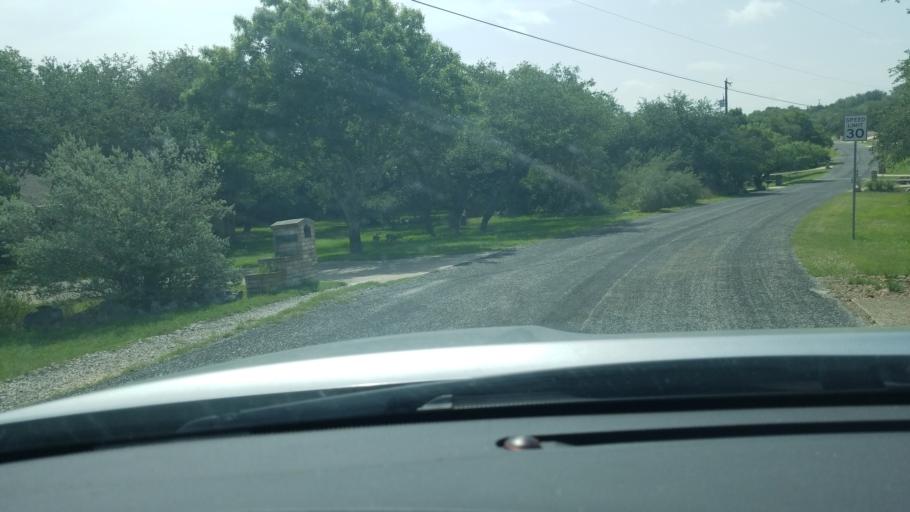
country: US
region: Texas
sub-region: Bexar County
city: Timberwood Park
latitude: 29.6900
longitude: -98.4948
